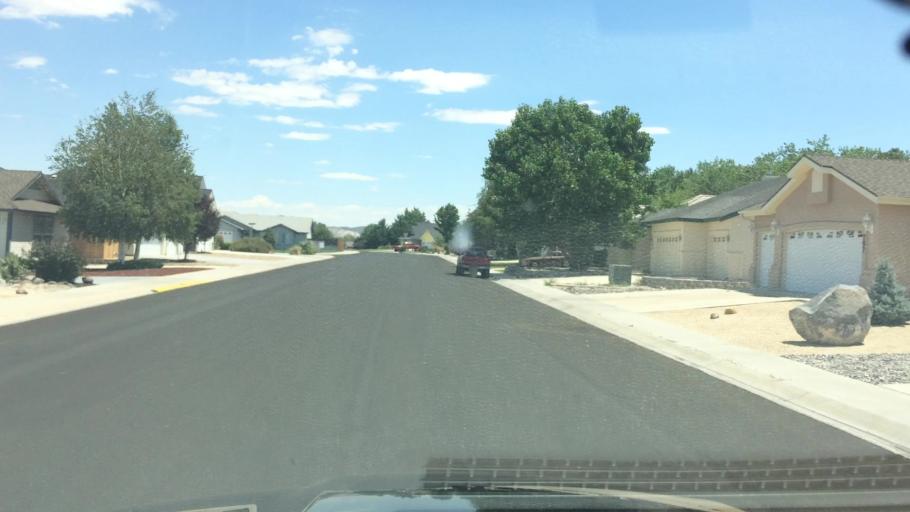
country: US
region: Nevada
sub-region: Lyon County
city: Fernley
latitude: 39.5843
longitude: -119.1485
